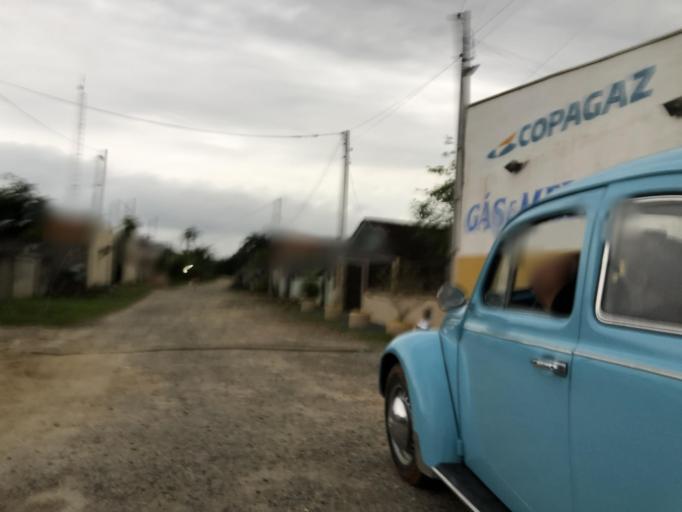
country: BR
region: Santa Catarina
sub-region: Sao Francisco Do Sul
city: Sao Francisco do Sul
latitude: -26.2225
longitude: -48.5312
